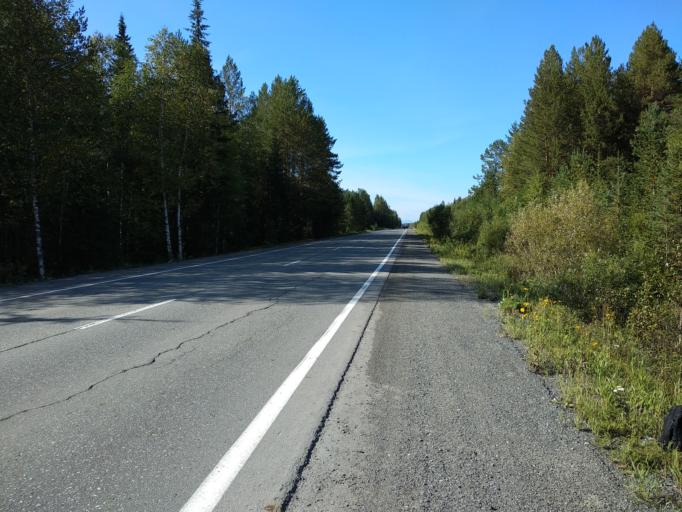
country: RU
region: Sverdlovsk
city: Volchansk
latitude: 60.0444
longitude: 60.0285
